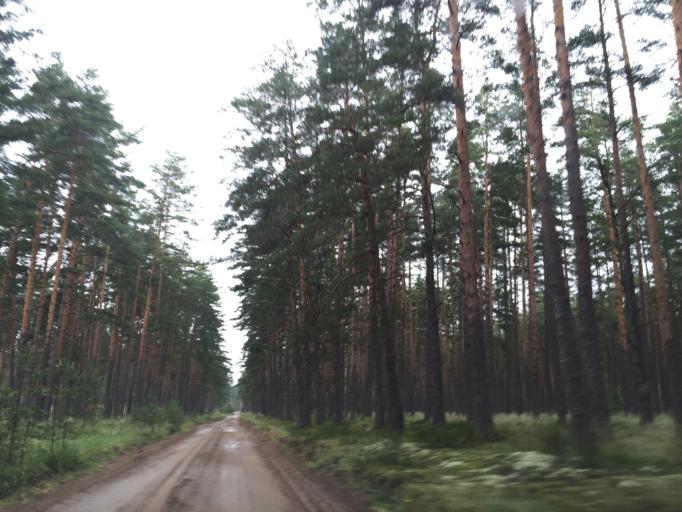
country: LV
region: Riga
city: Jaunciems
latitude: 57.0553
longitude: 24.2031
